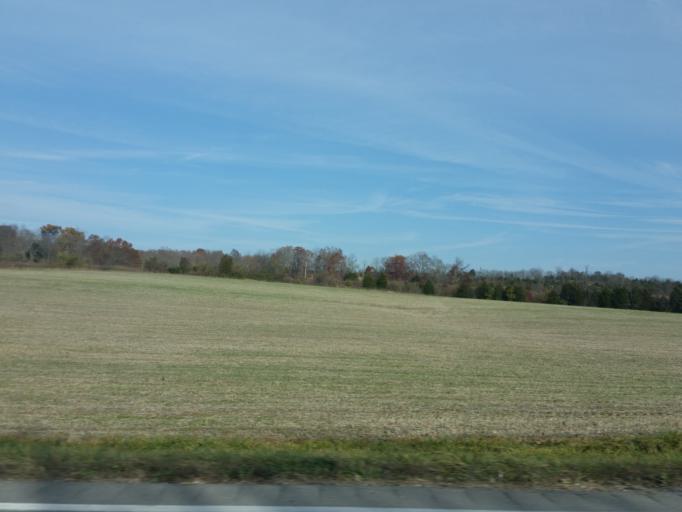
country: US
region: Kentucky
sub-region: Campbell County
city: Claryville
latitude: 38.8374
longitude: -84.3693
